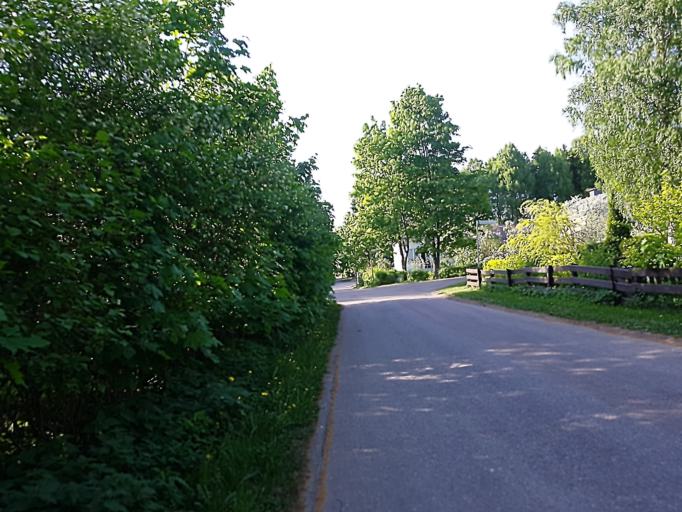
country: FI
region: Uusimaa
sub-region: Helsinki
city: Helsinki
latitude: 60.2460
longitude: 24.9319
